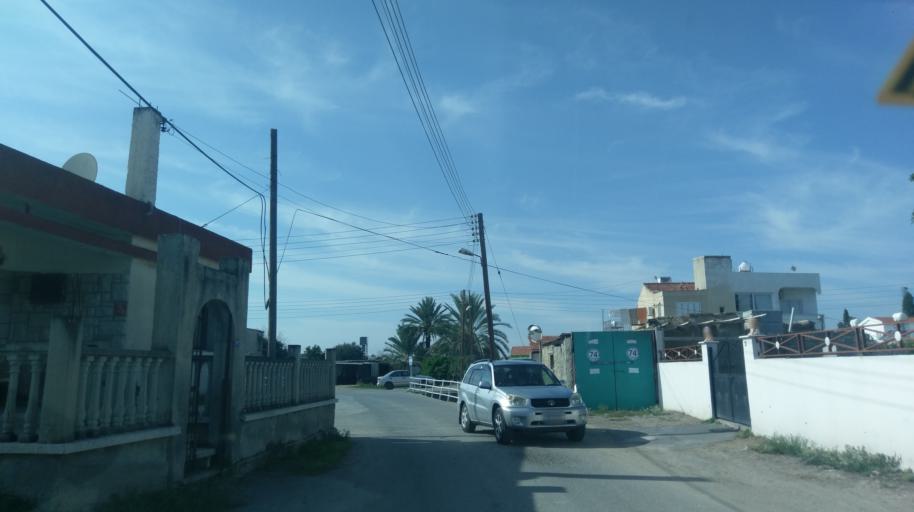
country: CY
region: Ammochostos
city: Lefkonoiko
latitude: 35.2530
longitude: 33.6873
